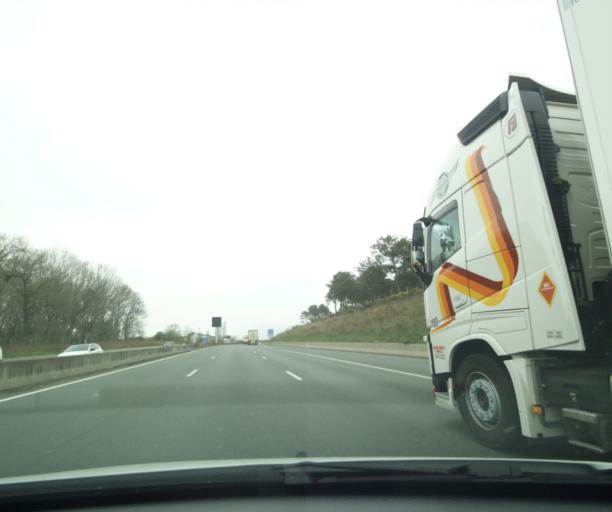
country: FR
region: Aquitaine
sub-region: Departement des Pyrenees-Atlantiques
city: Bassussarry
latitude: 43.4503
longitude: -1.5344
